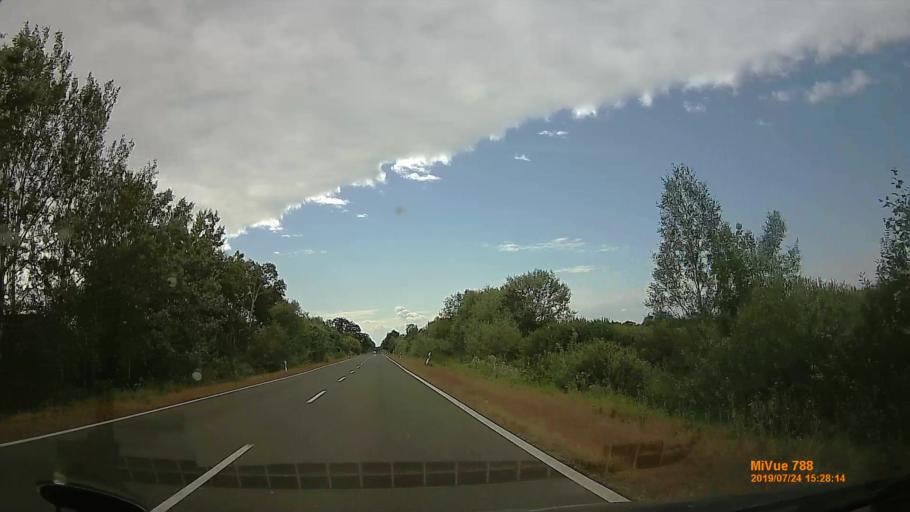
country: HU
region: Szabolcs-Szatmar-Bereg
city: Tarpa
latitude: 48.1609
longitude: 22.4820
